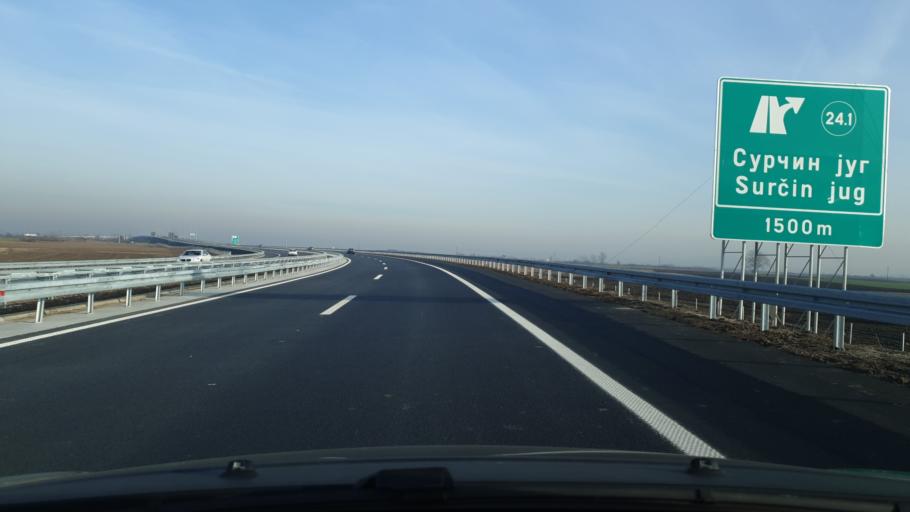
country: RS
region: Central Serbia
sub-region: Belgrade
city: Surcin
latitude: 44.7685
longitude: 20.2583
